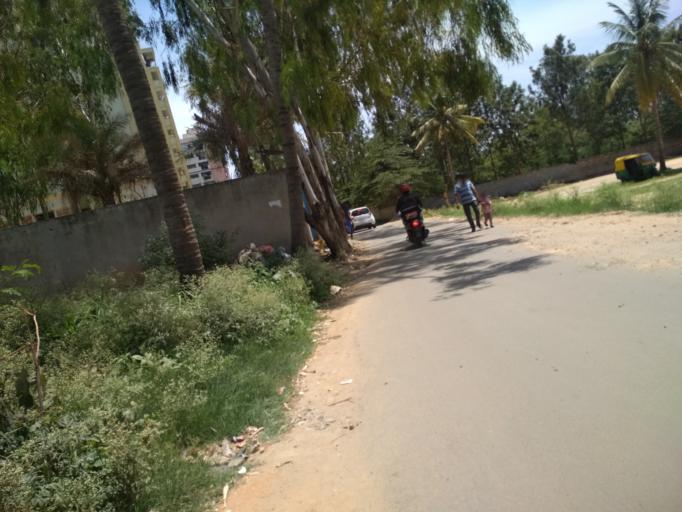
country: IN
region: Karnataka
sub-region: Bangalore Urban
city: Bangalore
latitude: 12.9299
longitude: 77.6711
